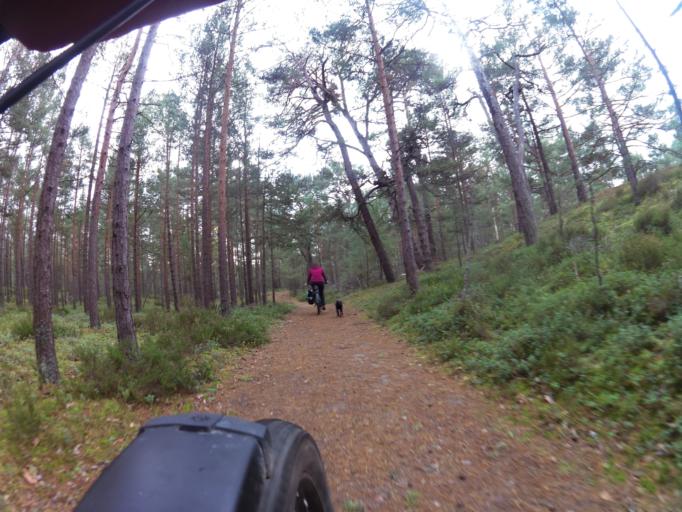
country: PL
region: Pomeranian Voivodeship
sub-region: Powiat pucki
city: Hel
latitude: 54.6245
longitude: 18.8032
